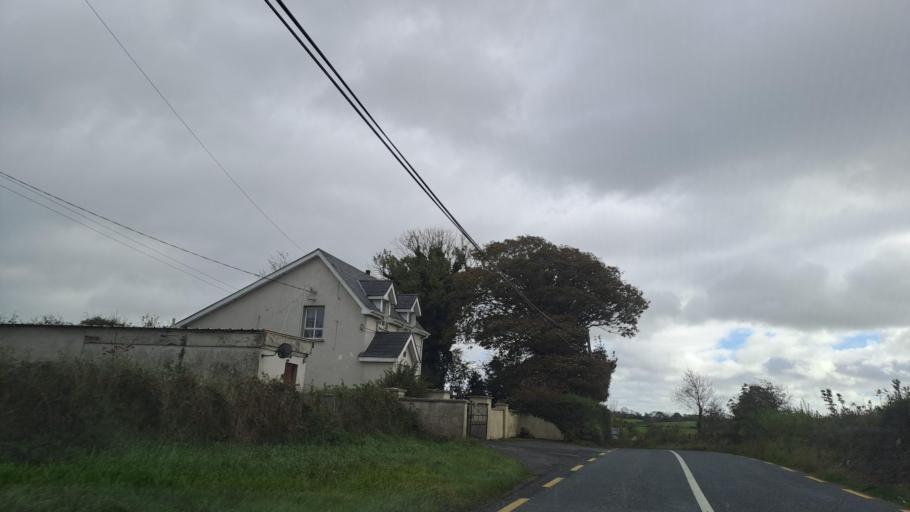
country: IE
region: Ulster
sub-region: An Cabhan
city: Kingscourt
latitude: 53.9111
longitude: -6.8447
